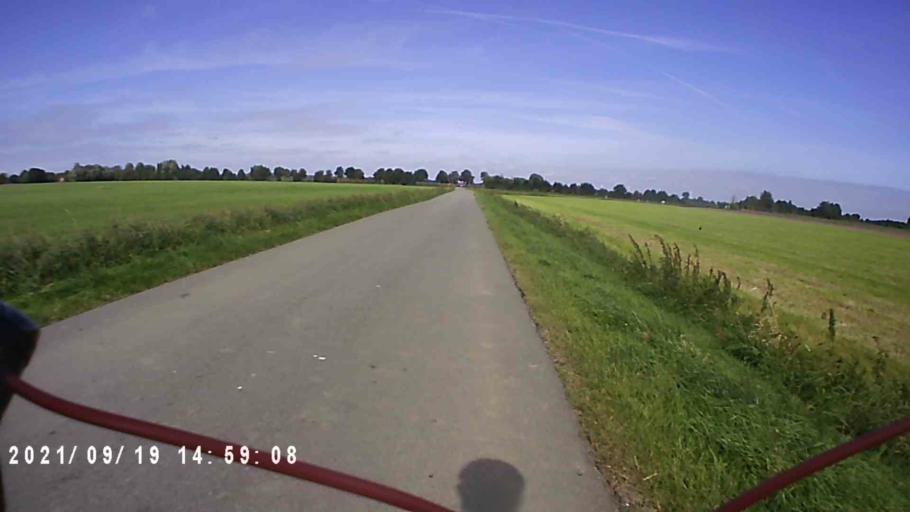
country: DE
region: Lower Saxony
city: Bunde
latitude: 53.1537
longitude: 7.2091
